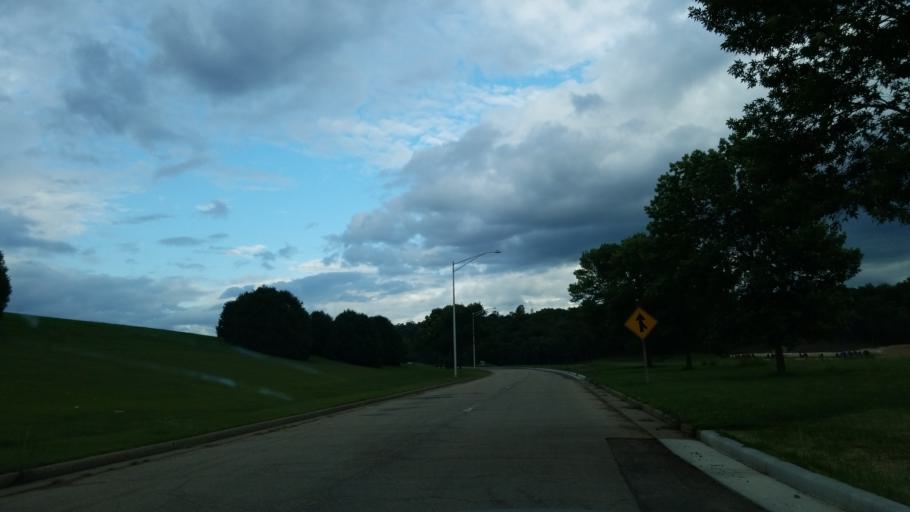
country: US
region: Minnesota
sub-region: Washington County
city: Lakeland
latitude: 44.9485
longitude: -92.7270
